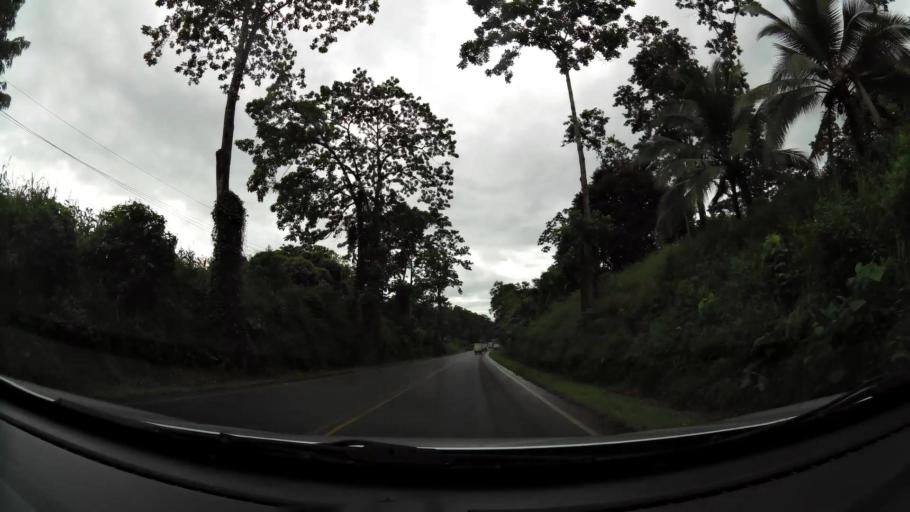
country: CR
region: Limon
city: Pocora
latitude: 10.1375
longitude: -83.5652
